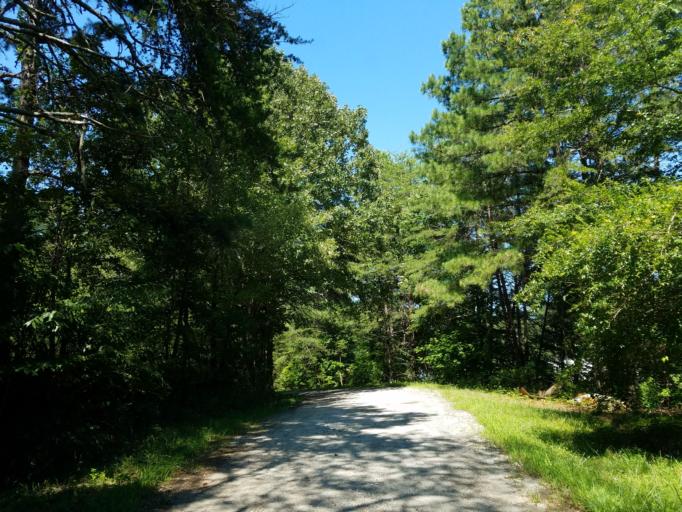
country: US
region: Georgia
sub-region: Lumpkin County
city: Dahlonega
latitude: 34.4226
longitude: -83.9934
